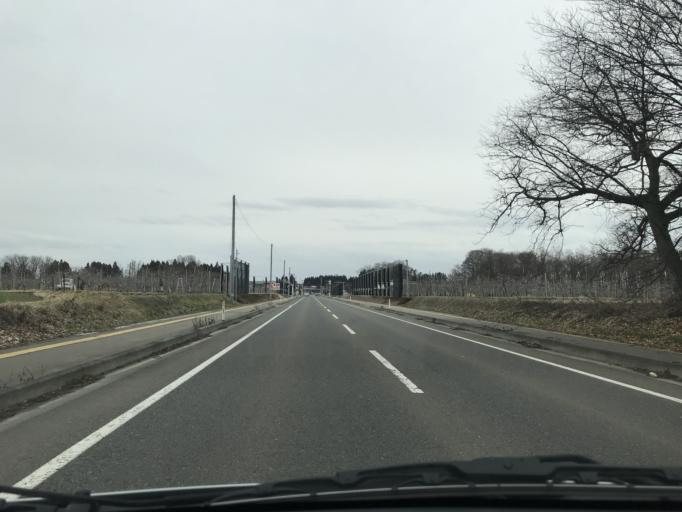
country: JP
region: Iwate
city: Hanamaki
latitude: 39.3630
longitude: 141.1107
